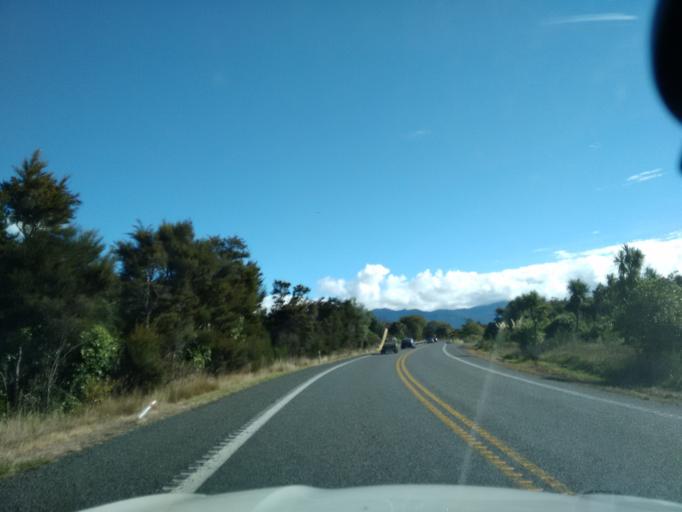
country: NZ
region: Waikato
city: Turangi
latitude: -38.9437
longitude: 175.8546
